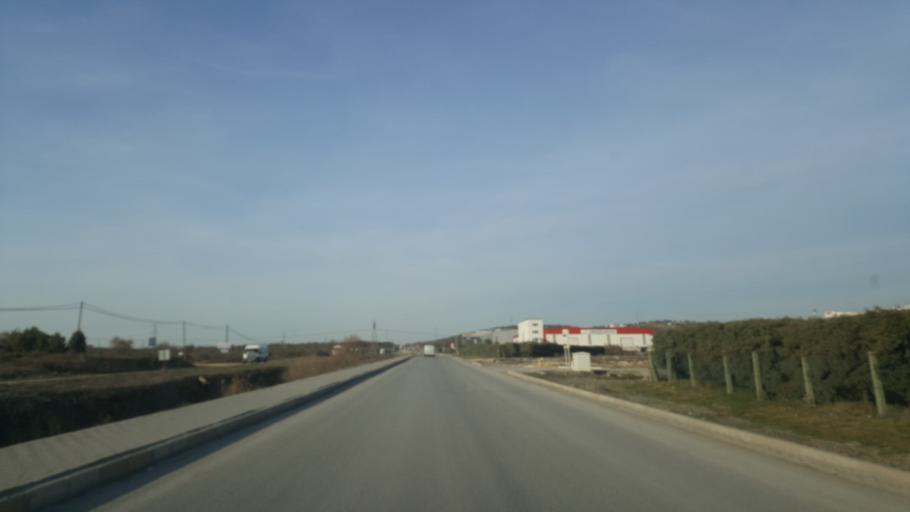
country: TR
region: Kocaeli
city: Tavsanli
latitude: 40.8567
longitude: 29.5566
